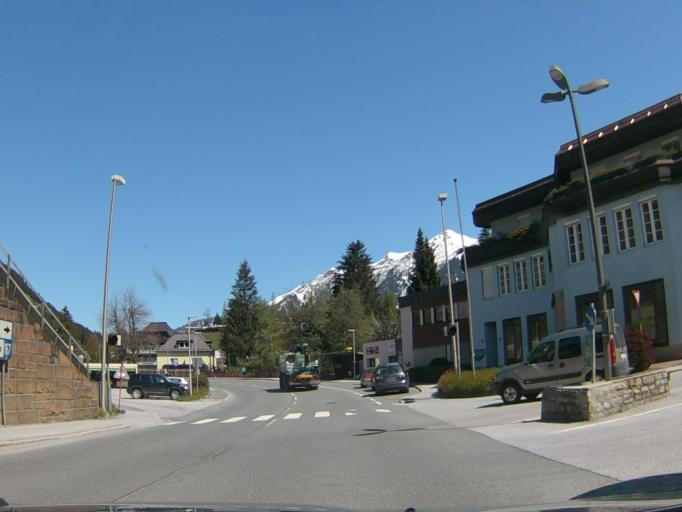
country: AT
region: Salzburg
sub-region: Politischer Bezirk Sankt Johann im Pongau
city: Bad Gastein
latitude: 47.1076
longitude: 13.1348
